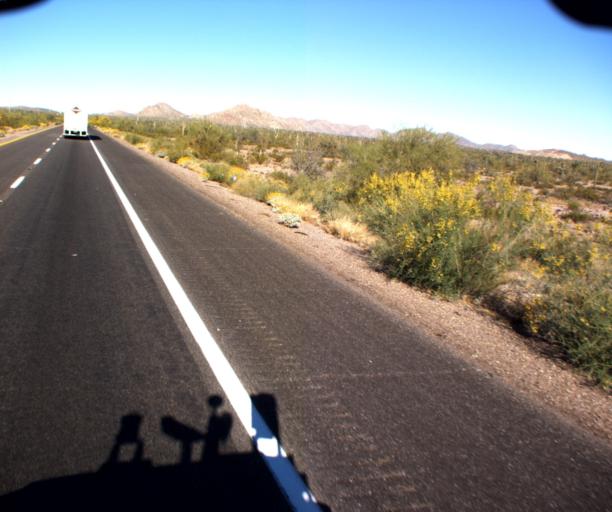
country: US
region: Arizona
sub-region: Pinal County
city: Maricopa
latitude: 32.8330
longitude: -112.0851
